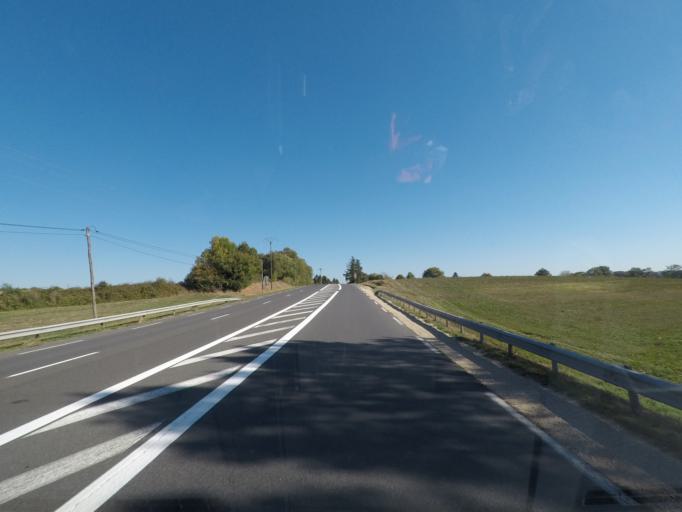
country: FR
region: Rhone-Alpes
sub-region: Departement de l'Ain
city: Saint-Paul-de-Varax
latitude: 46.0936
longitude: 5.1212
